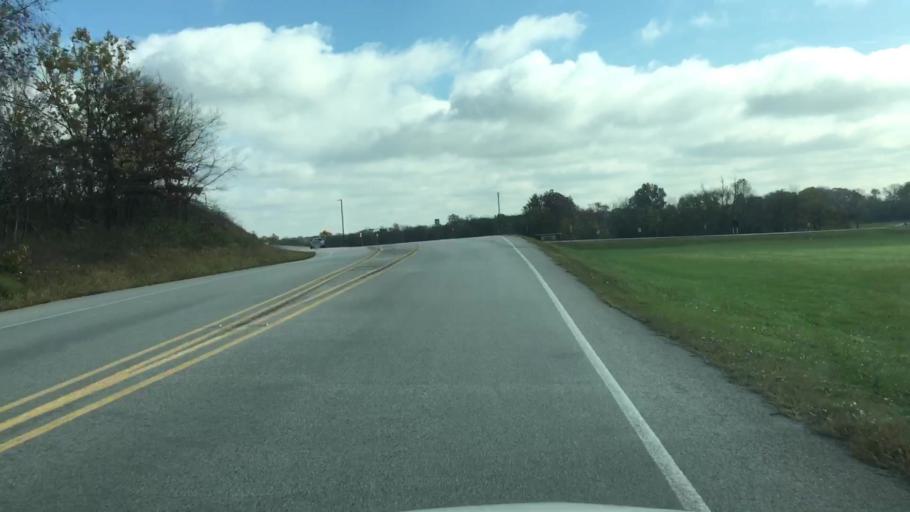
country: US
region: Arkansas
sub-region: Benton County
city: Centerton
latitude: 36.3010
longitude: -94.3085
